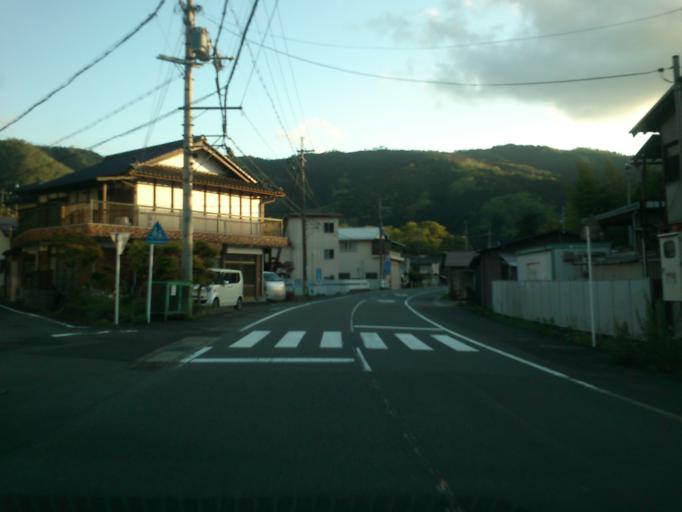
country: JP
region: Kyoto
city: Ayabe
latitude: 35.2649
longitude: 135.3996
